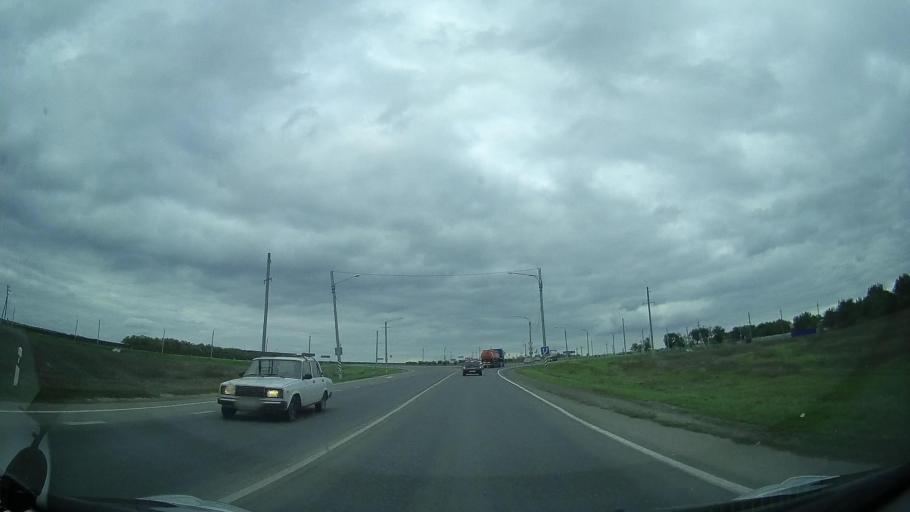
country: RU
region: Rostov
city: Yegorlykskaya
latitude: 46.5650
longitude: 40.6293
